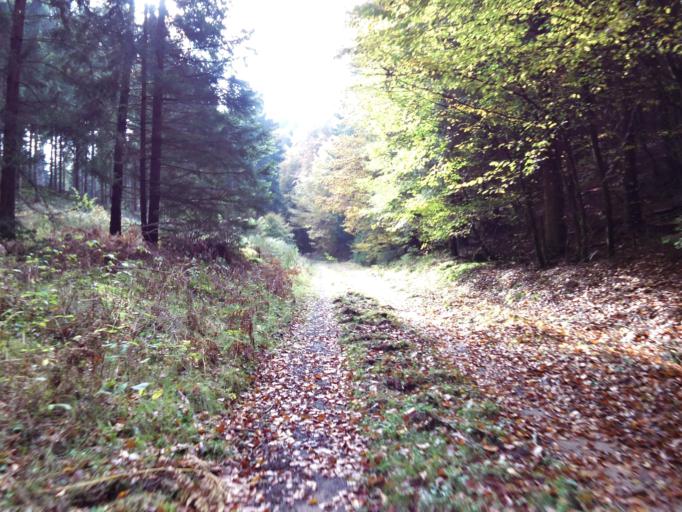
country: DE
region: Rheinland-Pfalz
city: Fischbach
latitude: 49.4734
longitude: 7.9520
